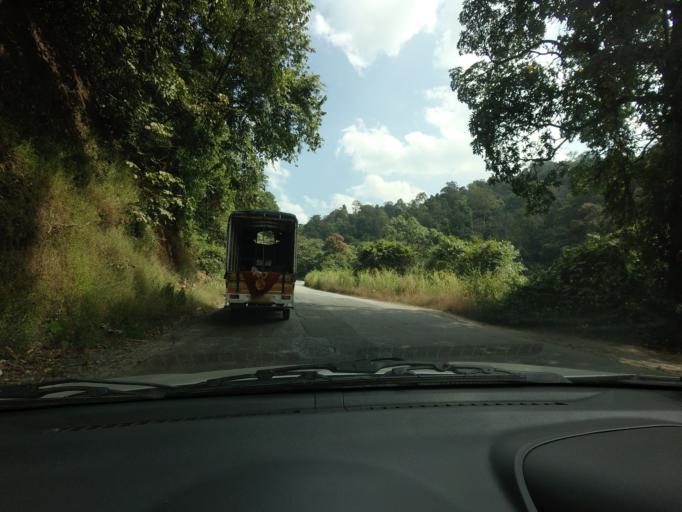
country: IN
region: Karnataka
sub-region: Hassan
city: Sakleshpur
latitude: 12.8293
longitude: 75.6309
